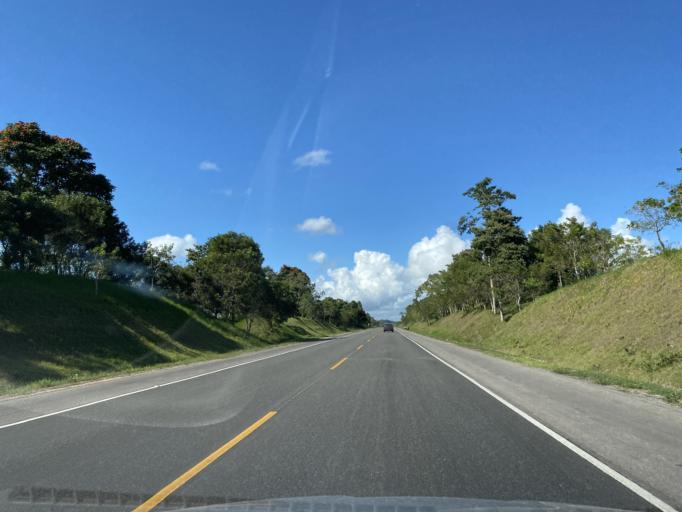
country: DO
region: Monte Plata
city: Sabana Grande de Boya
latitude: 18.9915
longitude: -69.8135
